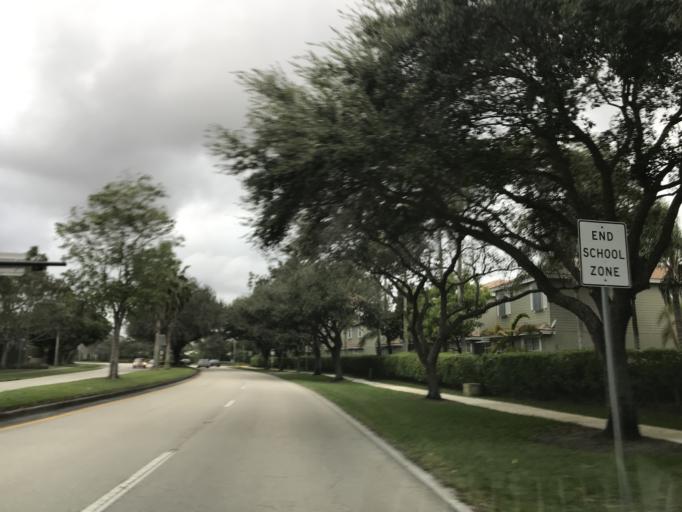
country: US
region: Florida
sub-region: Broward County
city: Coral Springs
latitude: 26.2994
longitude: -80.2687
